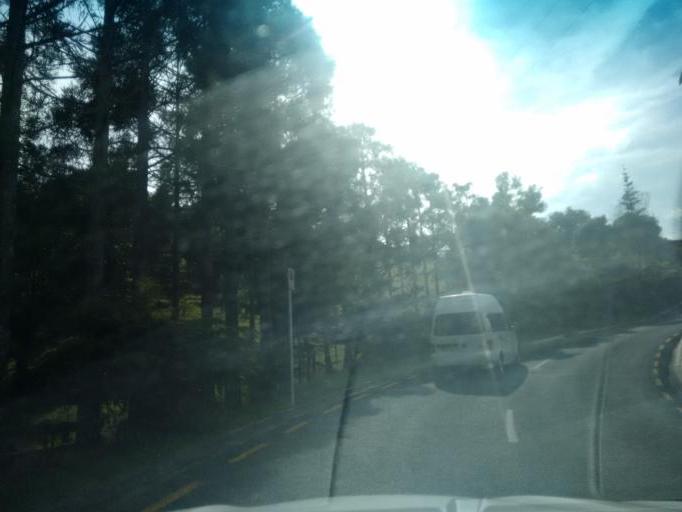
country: NZ
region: Waikato
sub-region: Thames-Coromandel District
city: Whitianga
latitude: -36.8387
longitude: 175.7984
